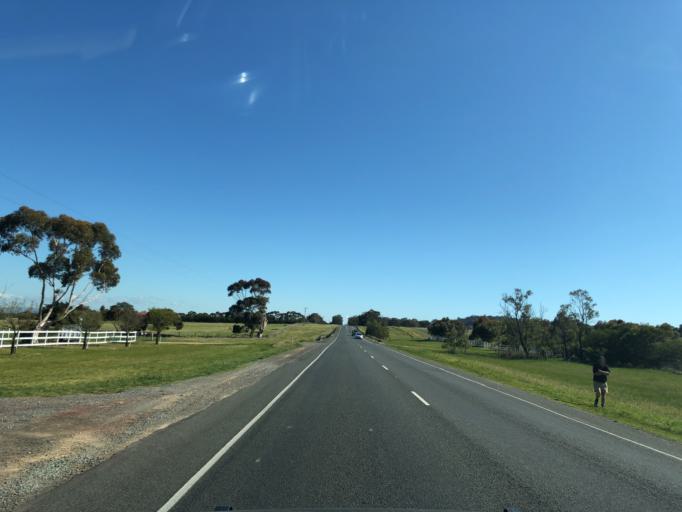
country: AU
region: Victoria
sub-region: Melton
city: Kurunjang
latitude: -37.6106
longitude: 144.5778
